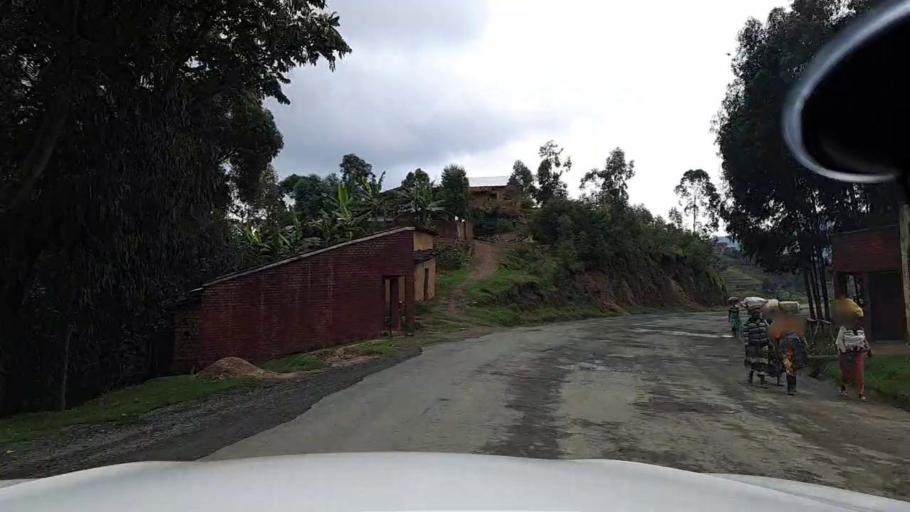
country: RW
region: Western Province
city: Kibuye
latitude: -2.0584
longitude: 29.5242
